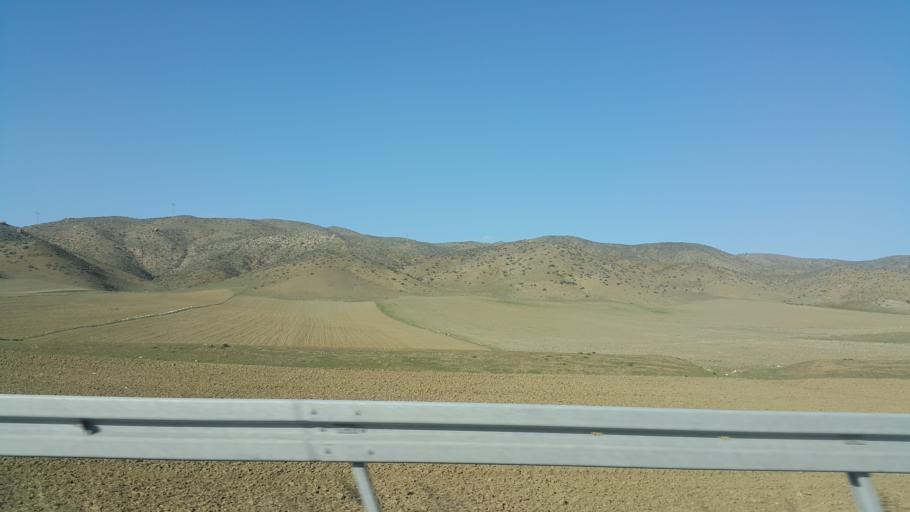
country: TR
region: Ankara
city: Sereflikochisar
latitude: 38.8089
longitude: 33.6102
